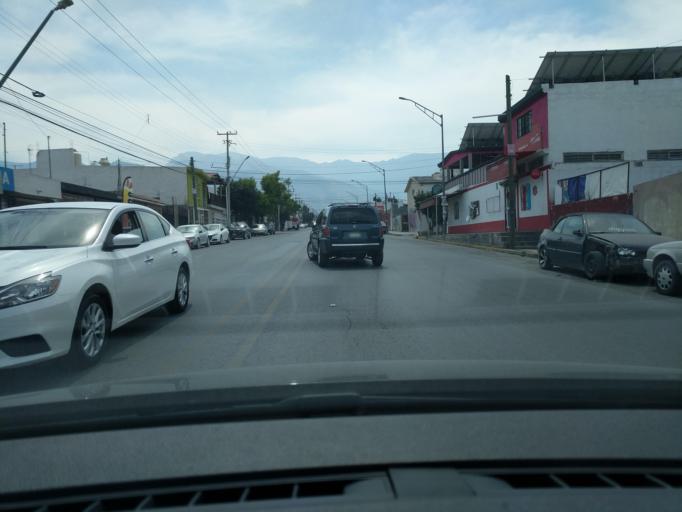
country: MX
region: Coahuila
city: Saltillo
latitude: 25.4142
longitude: -100.9421
